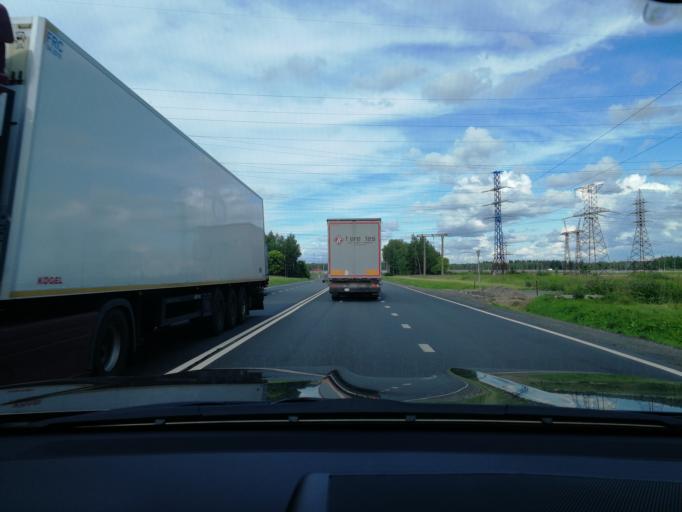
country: RU
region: Moskovskaya
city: Mikhnevo
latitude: 55.0755
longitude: 37.9259
